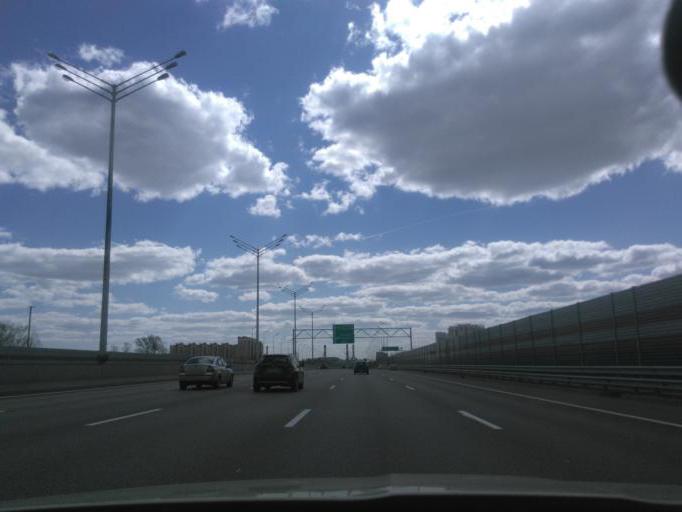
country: RU
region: Moskovskaya
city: Levoberezhnaya
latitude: 55.9108
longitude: 37.4692
